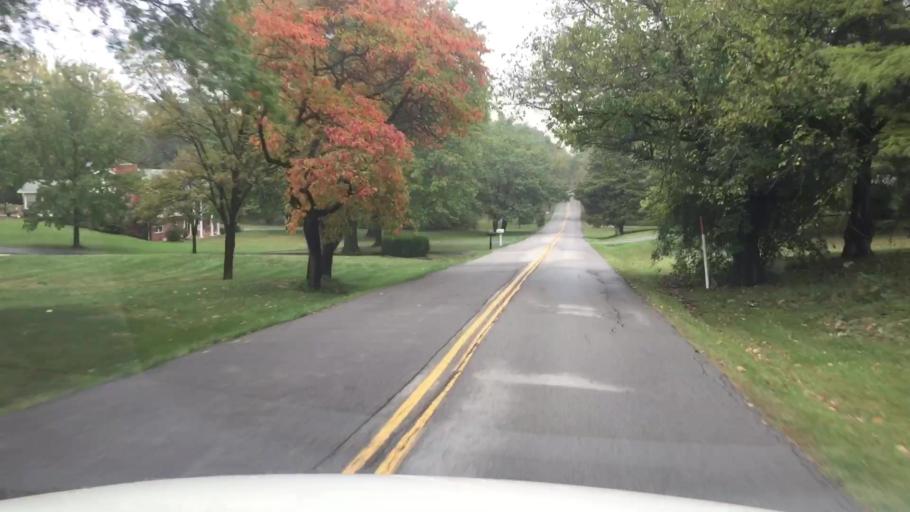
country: US
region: Missouri
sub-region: Boone County
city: Columbia
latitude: 38.8584
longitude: -92.3150
